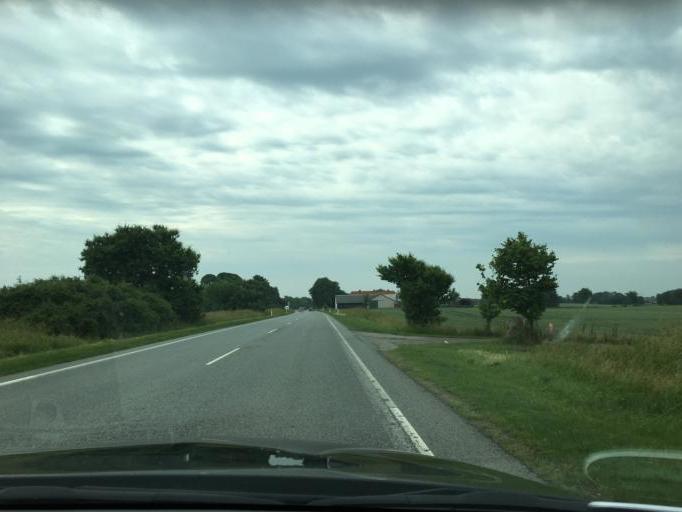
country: DK
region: South Denmark
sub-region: Kolding Kommune
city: Kolding
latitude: 55.5952
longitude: 9.4937
